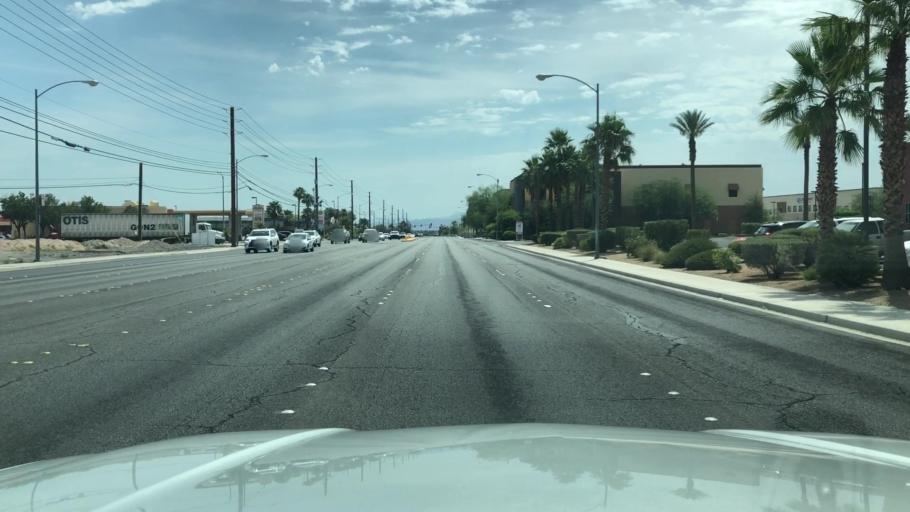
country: US
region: Nevada
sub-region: Clark County
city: Paradise
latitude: 36.0568
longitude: -115.1600
